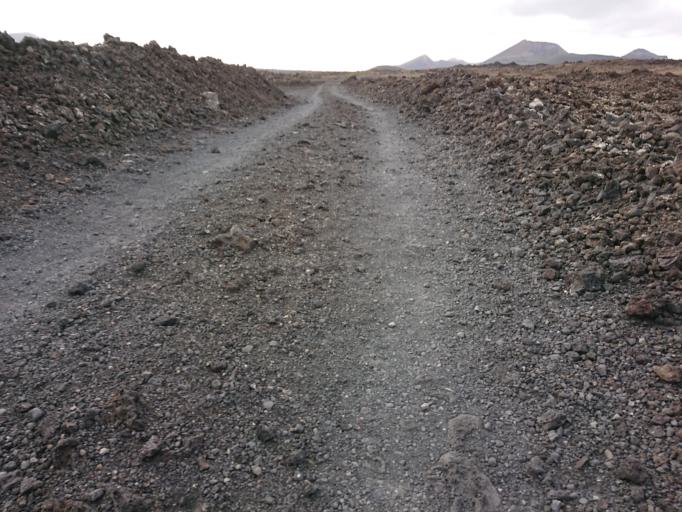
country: ES
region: Canary Islands
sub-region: Provincia de Las Palmas
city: Tias
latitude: 29.0021
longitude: -13.6866
